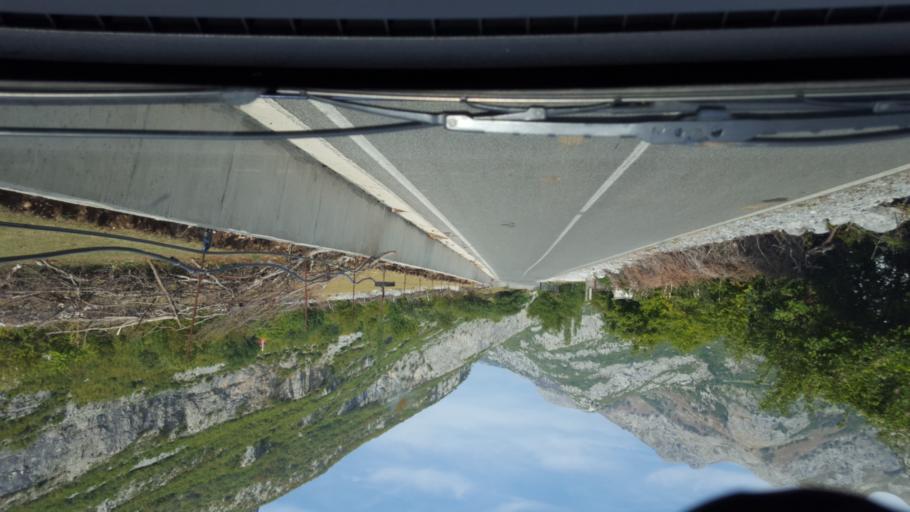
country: AL
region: Shkoder
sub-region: Rrethi i Malesia e Madhe
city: Kastrat
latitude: 42.5123
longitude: 19.6187
